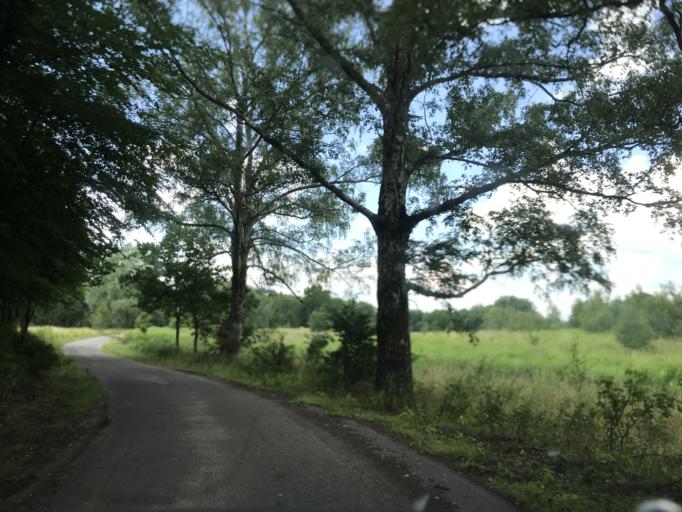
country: PL
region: West Pomeranian Voivodeship
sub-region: Powiat stargardzki
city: Insko
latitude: 53.4910
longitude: 15.4999
